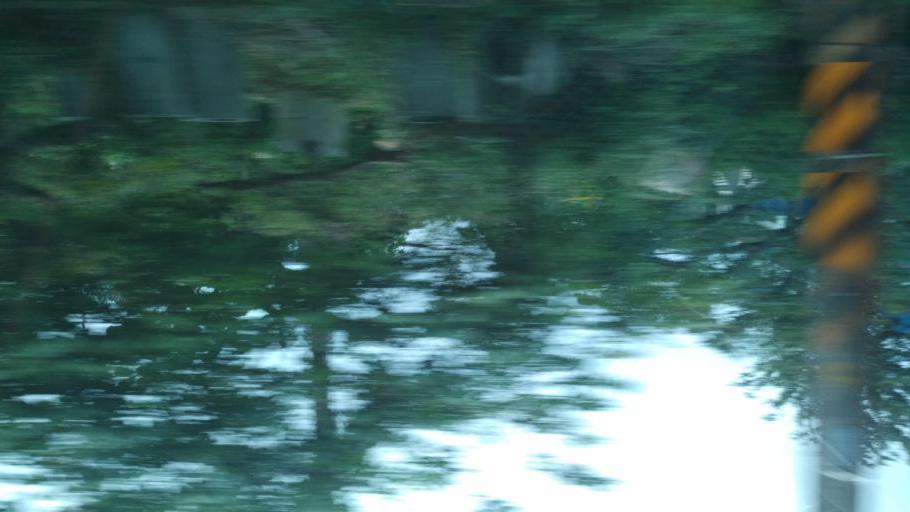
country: TW
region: Taiwan
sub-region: Keelung
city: Keelung
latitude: 25.2089
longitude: 121.6512
